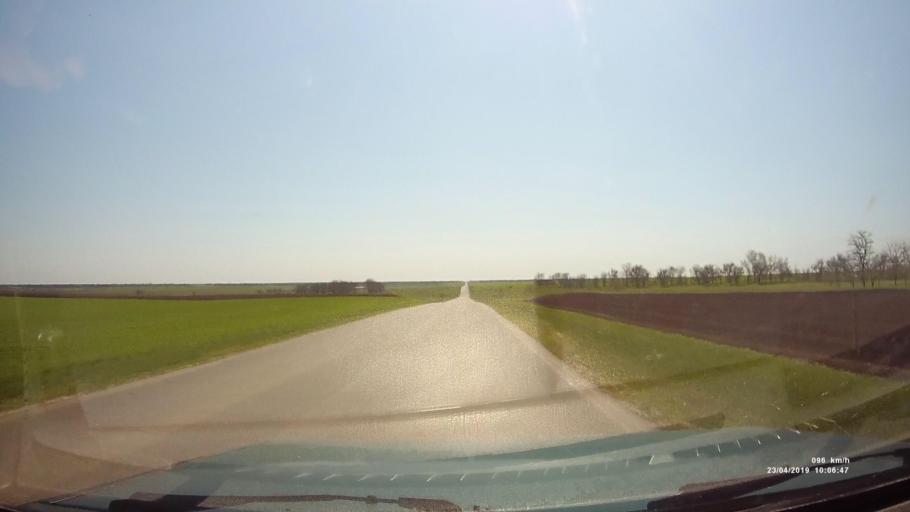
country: RU
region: Rostov
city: Sovetskoye
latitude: 46.7312
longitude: 42.2413
